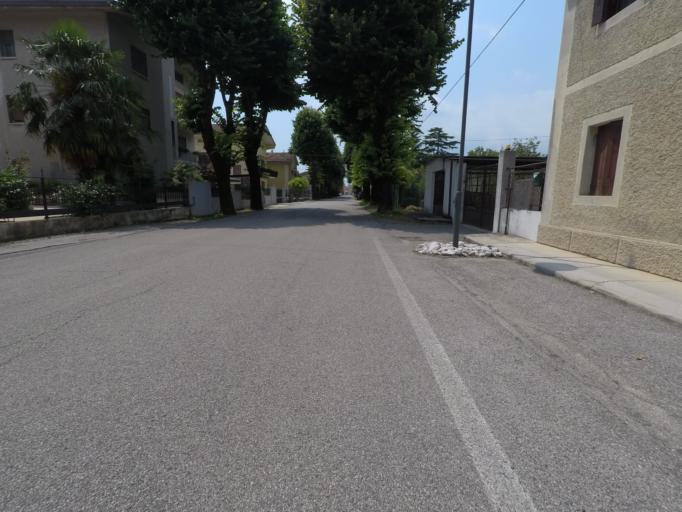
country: IT
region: Friuli Venezia Giulia
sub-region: Provincia di Pordenone
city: Aviano-Castello
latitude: 46.0636
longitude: 12.5825
